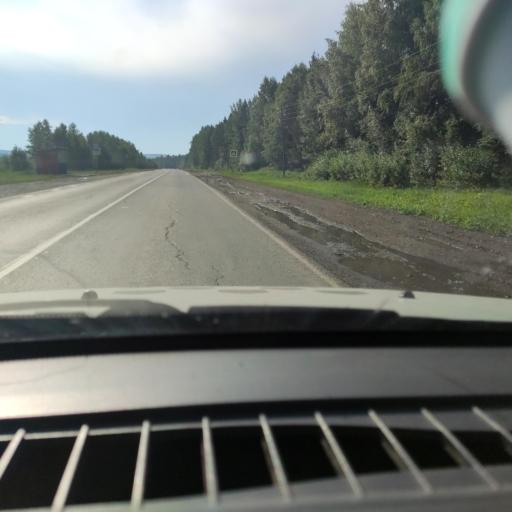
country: RU
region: Kirov
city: Kostino
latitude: 58.8577
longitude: 53.1848
